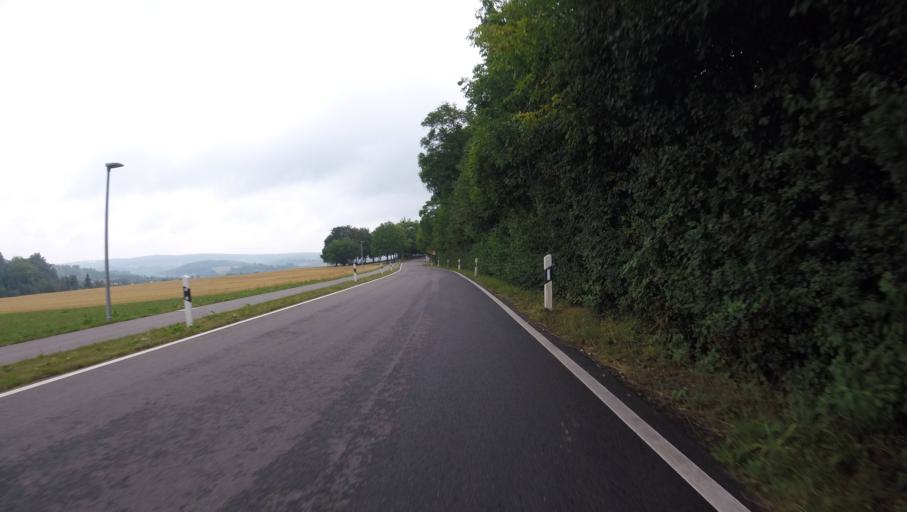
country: DE
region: Baden-Wuerttemberg
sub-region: Regierungsbezirk Stuttgart
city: Oppenweiler
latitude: 48.9760
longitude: 9.4455
